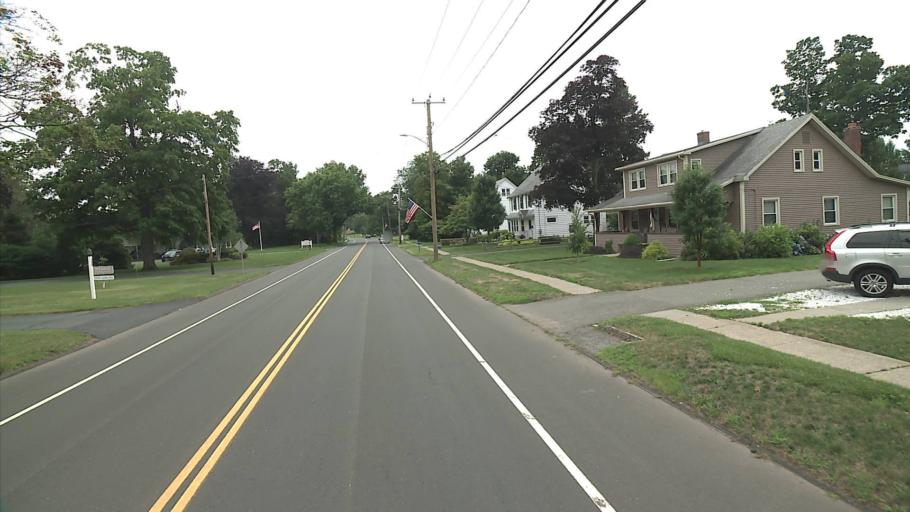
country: US
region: Connecticut
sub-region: Middlesex County
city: Cromwell
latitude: 41.6147
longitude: -72.6528
